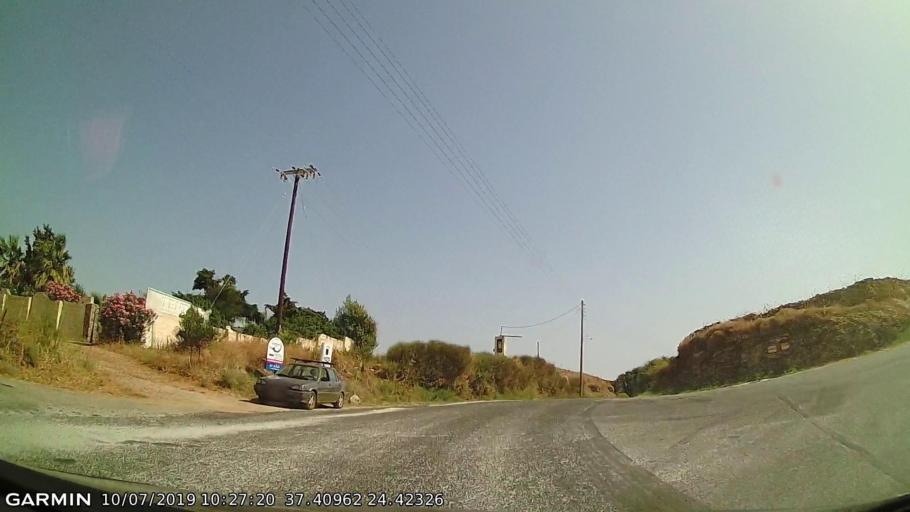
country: GR
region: South Aegean
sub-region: Nomos Kykladon
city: Kythnos
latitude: 37.4093
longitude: 24.4237
